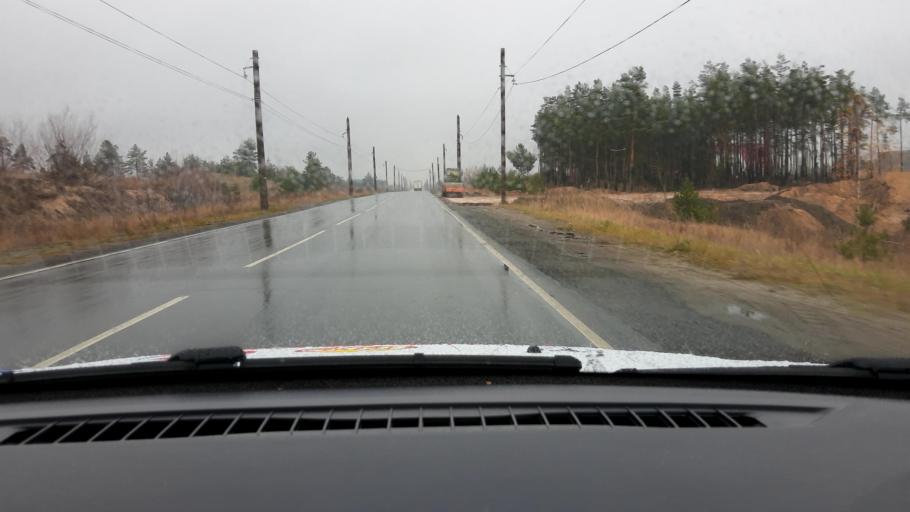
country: RU
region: Nizjnij Novgorod
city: Dzerzhinsk
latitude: 56.2597
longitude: 43.5146
